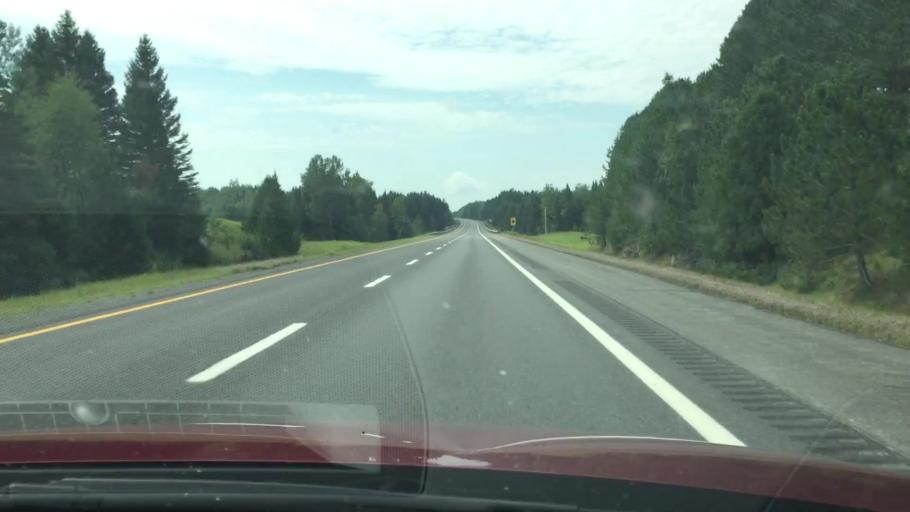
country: US
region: Maine
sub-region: Aroostook County
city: Hodgdon
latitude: 46.1394
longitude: -68.0744
